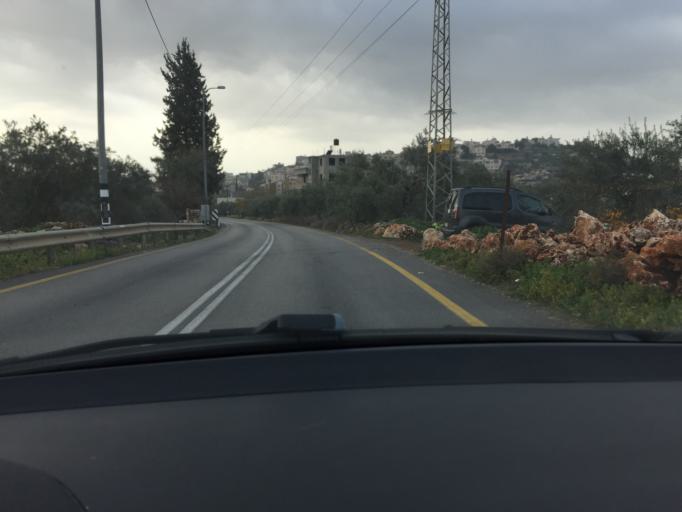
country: PS
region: West Bank
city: Al Lubban al Gharbi
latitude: 32.0408
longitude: 35.0407
